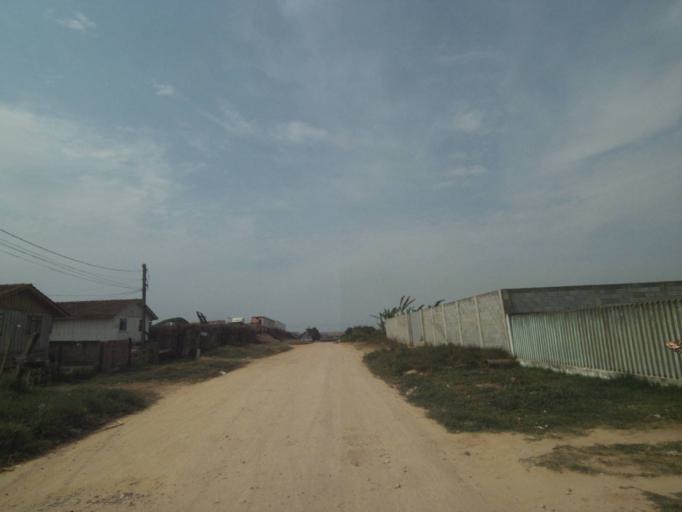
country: BR
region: Parana
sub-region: Pinhais
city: Pinhais
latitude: -25.4730
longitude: -49.2131
